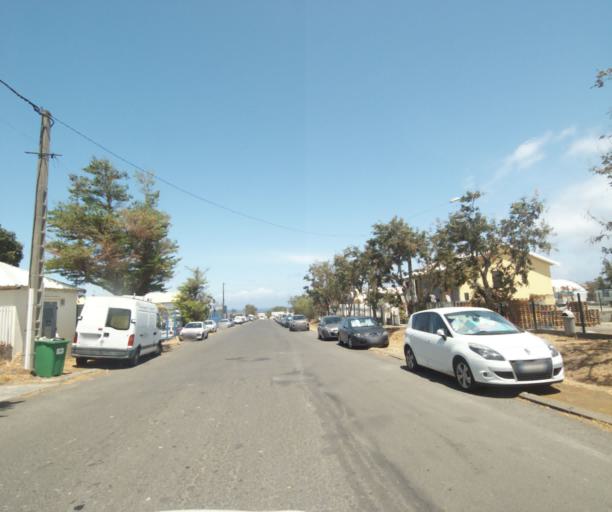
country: RE
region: Reunion
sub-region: Reunion
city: Le Port
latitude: -20.9638
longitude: 55.2964
